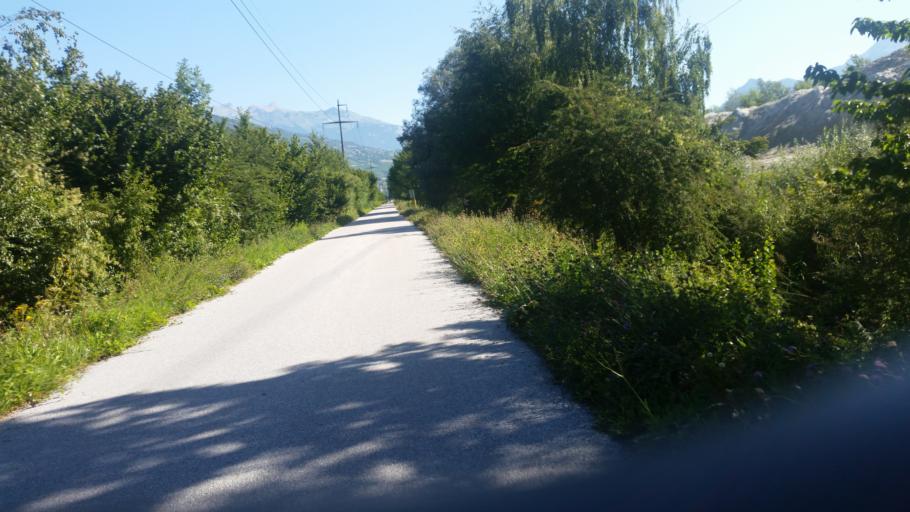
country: CH
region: Valais
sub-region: Sion District
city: Saint-Leonard
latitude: 46.2435
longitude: 7.4261
